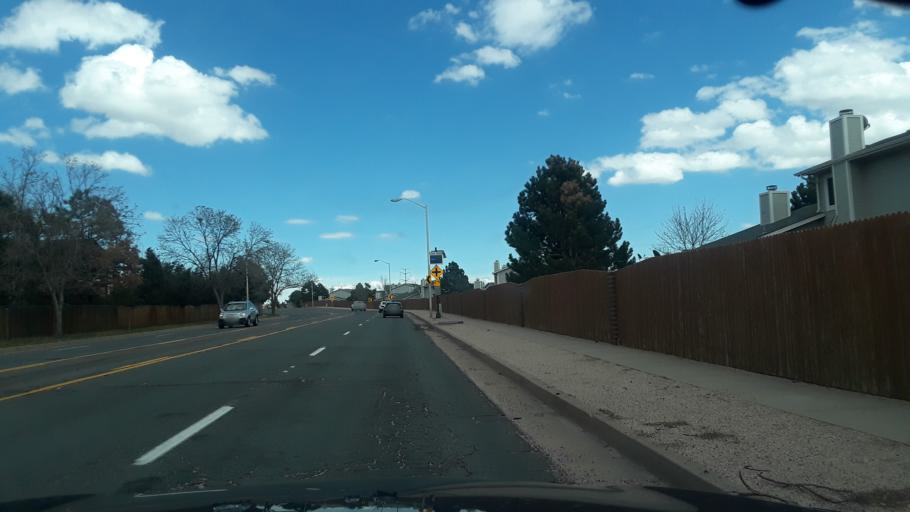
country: US
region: Colorado
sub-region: El Paso County
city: Black Forest
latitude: 38.9420
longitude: -104.7682
